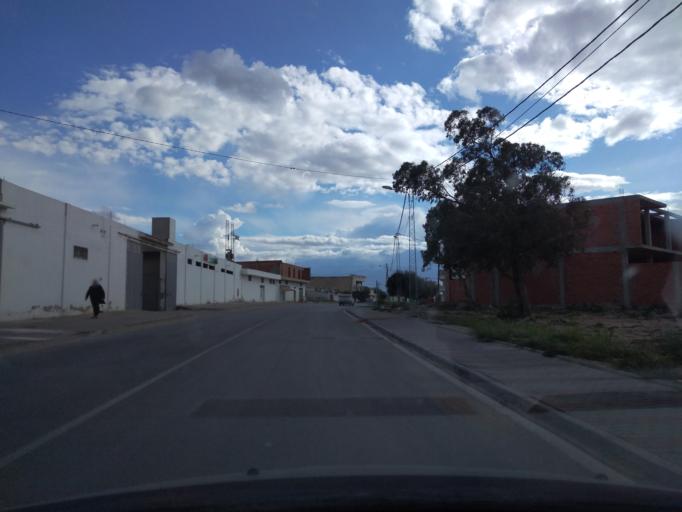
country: TN
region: Susah
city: Masakin
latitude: 35.7171
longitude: 10.5641
